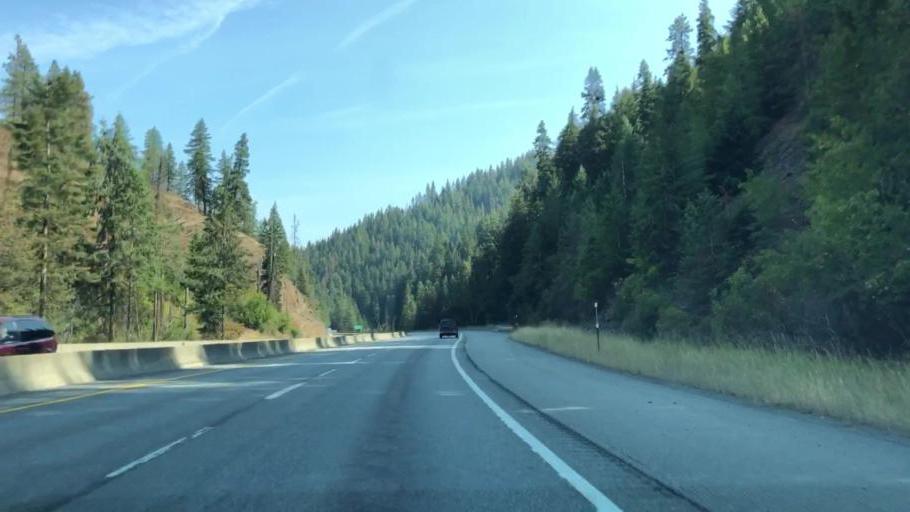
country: US
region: Idaho
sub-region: Kootenai County
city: Coeur d'Alene
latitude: 47.6295
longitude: -116.5995
